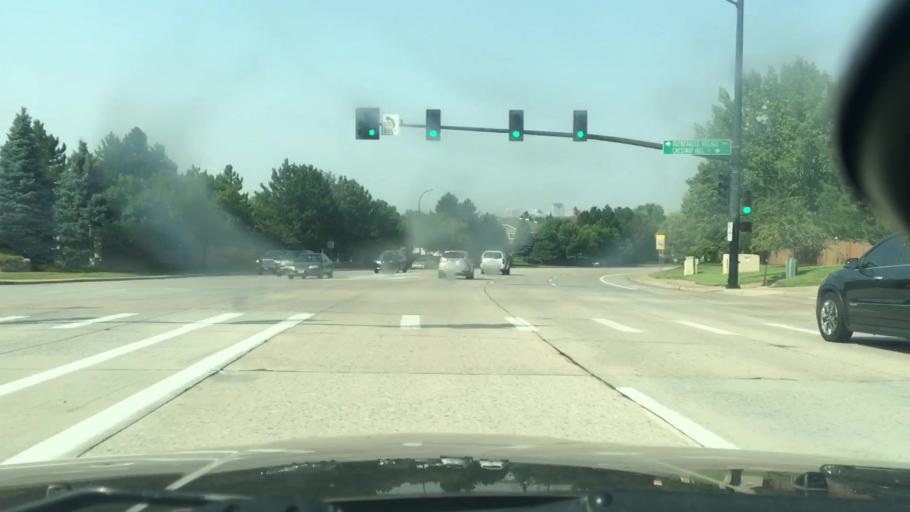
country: US
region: Colorado
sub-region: Douglas County
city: Acres Green
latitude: 39.5549
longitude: -104.9116
